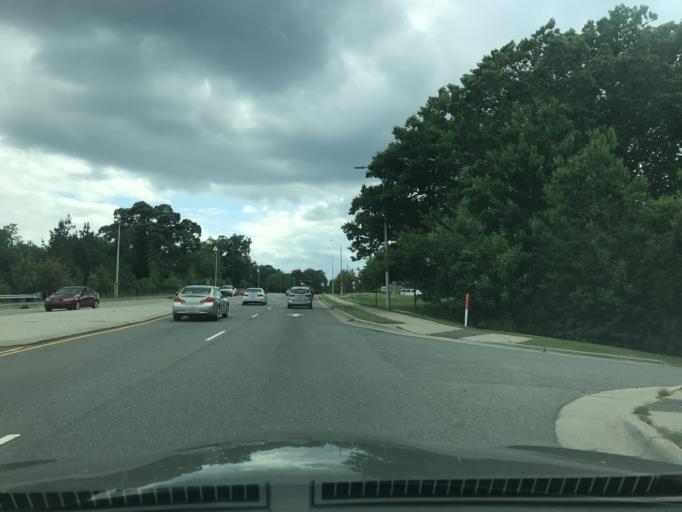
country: US
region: North Carolina
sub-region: Wake County
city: Wake Forest
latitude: 35.9336
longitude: -78.5789
